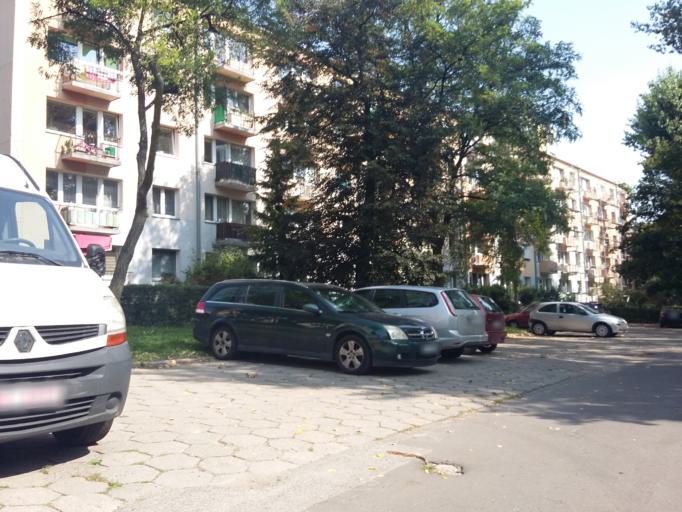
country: PL
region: Lodz Voivodeship
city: Lodz
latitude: 51.7442
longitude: 19.4149
